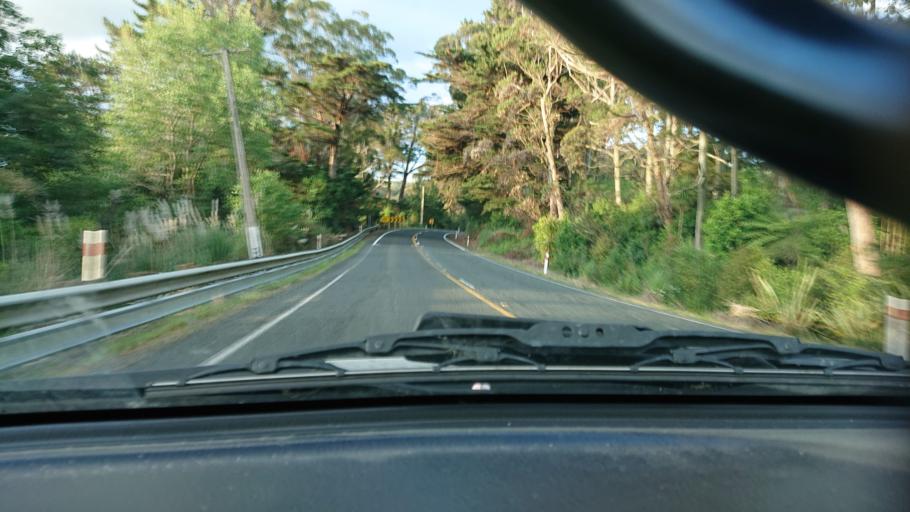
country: NZ
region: Auckland
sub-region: Auckland
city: Parakai
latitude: -36.5383
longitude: 174.4558
